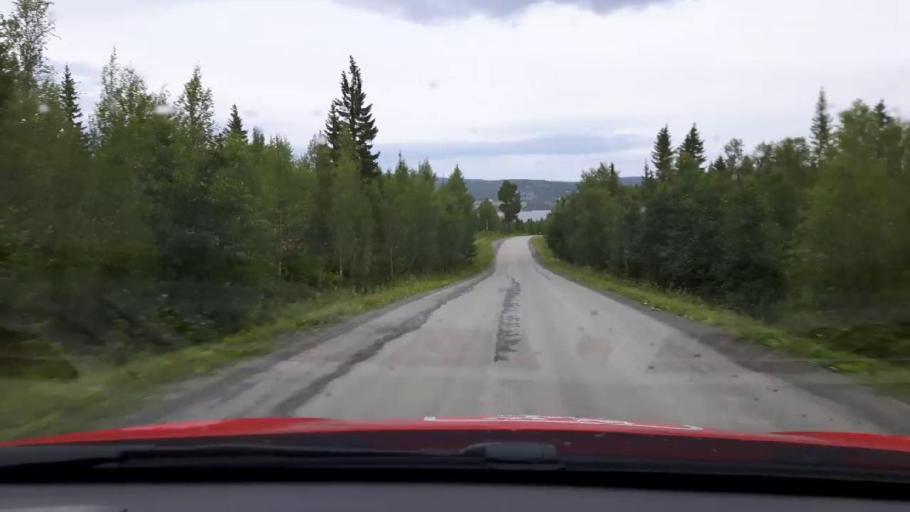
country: SE
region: Jaemtland
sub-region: Are Kommun
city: Are
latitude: 63.4379
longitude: 13.2112
